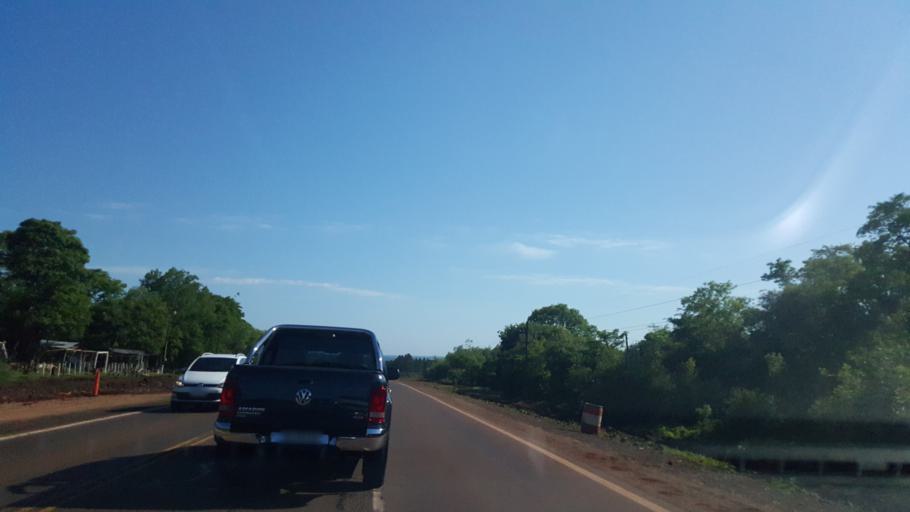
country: AR
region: Misiones
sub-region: Departamento de Candelaria
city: Loreto
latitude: -27.3497
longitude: -55.5479
